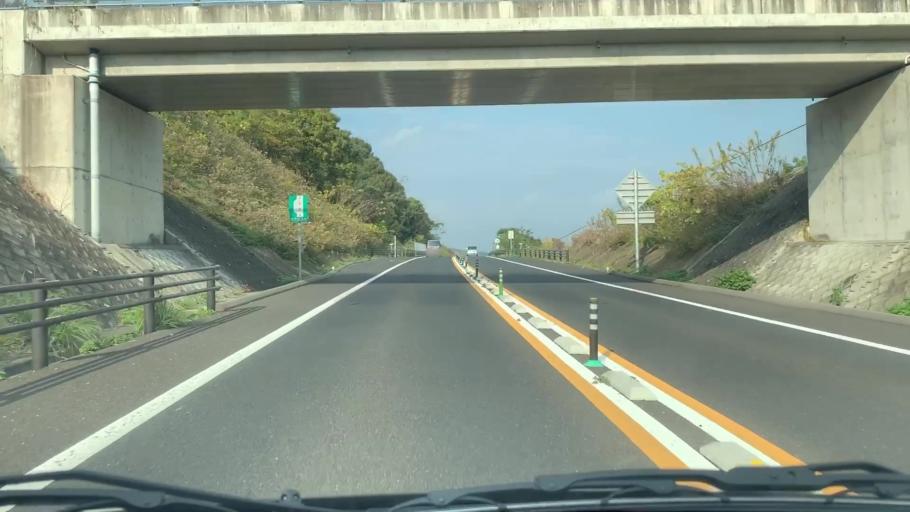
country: JP
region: Nagasaki
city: Sasebo
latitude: 33.0066
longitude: 129.7277
